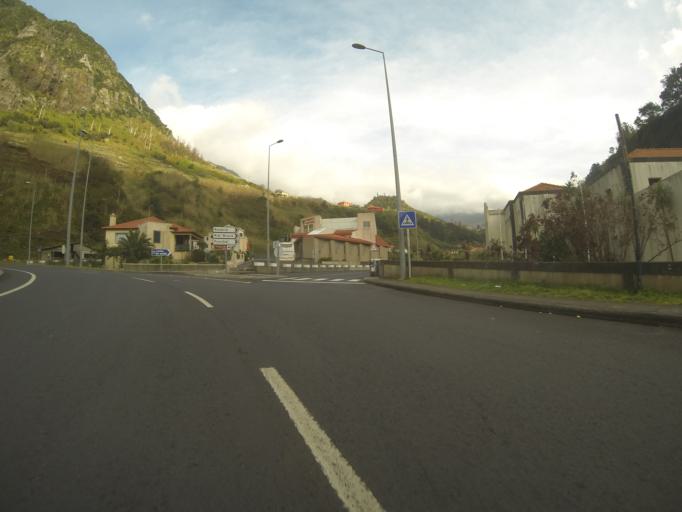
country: PT
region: Madeira
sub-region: Sao Vicente
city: Sao Vicente
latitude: 32.8019
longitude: -17.0439
